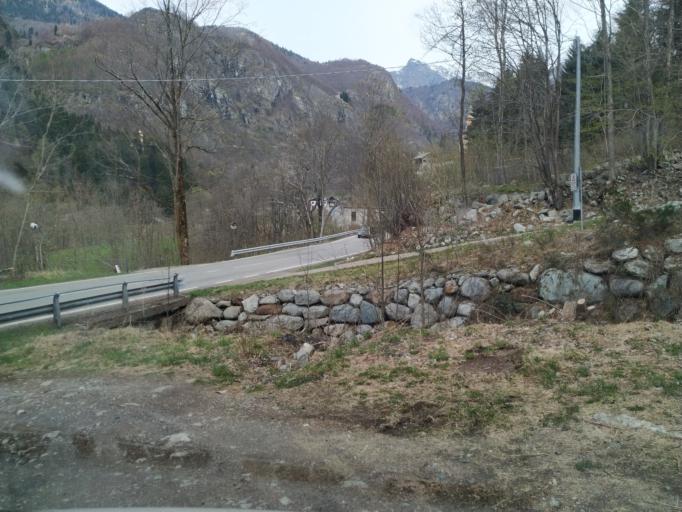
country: IT
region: Piedmont
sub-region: Provincia di Vercelli
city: Campertogno
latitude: 45.7920
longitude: 8.0377
